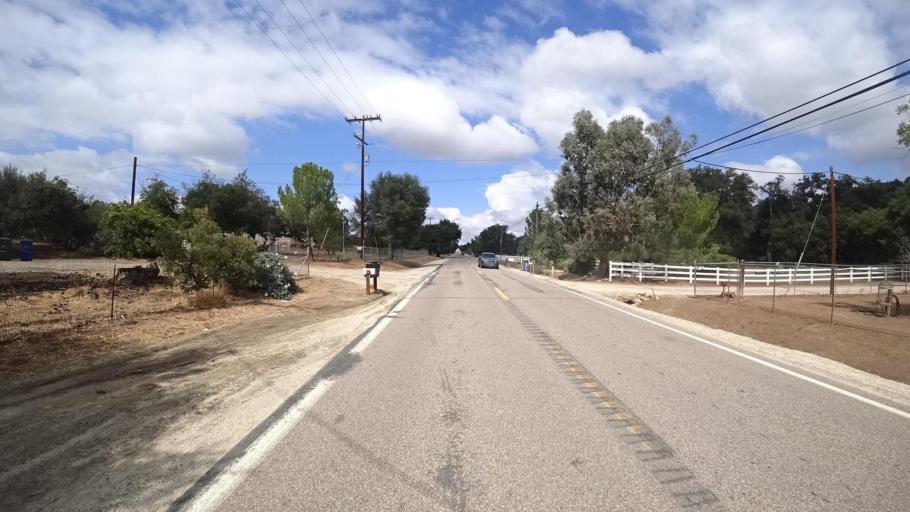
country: US
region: California
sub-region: San Diego County
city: Campo
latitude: 32.6624
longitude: -116.4880
